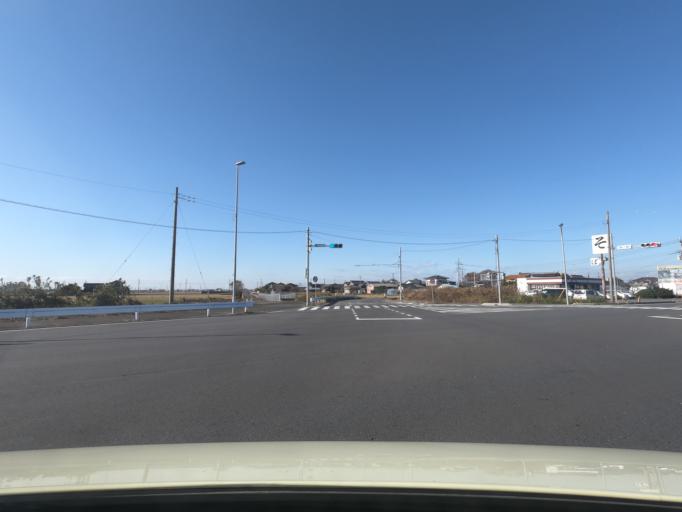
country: JP
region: Ibaraki
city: Ishige
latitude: 36.1588
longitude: 139.9955
